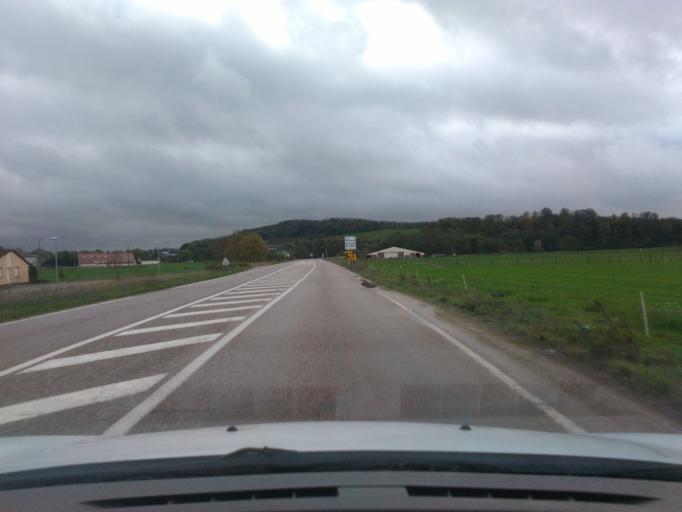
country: FR
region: Lorraine
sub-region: Departement des Vosges
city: Charmes
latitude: 48.3787
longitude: 6.2698
